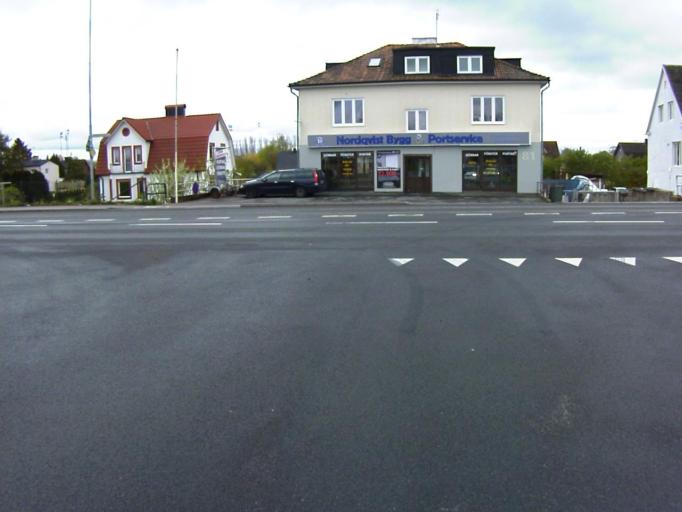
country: SE
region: Skane
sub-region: Kristianstads Kommun
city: Kristianstad
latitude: 56.0208
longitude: 14.1363
